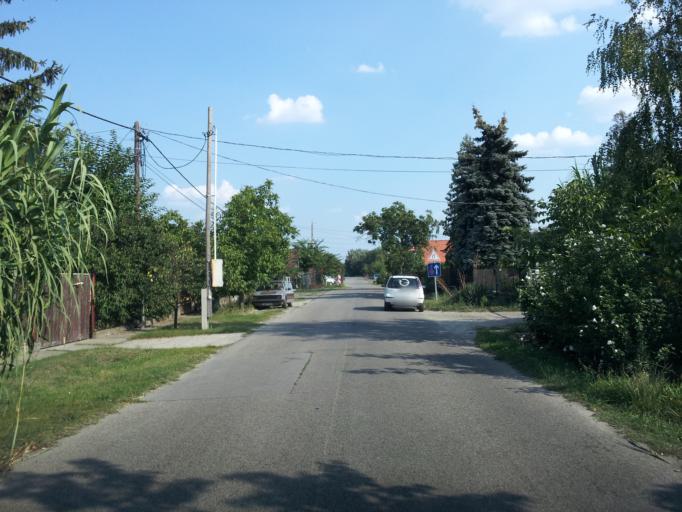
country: HU
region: Pest
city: Szigethalom
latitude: 47.3158
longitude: 19.0031
